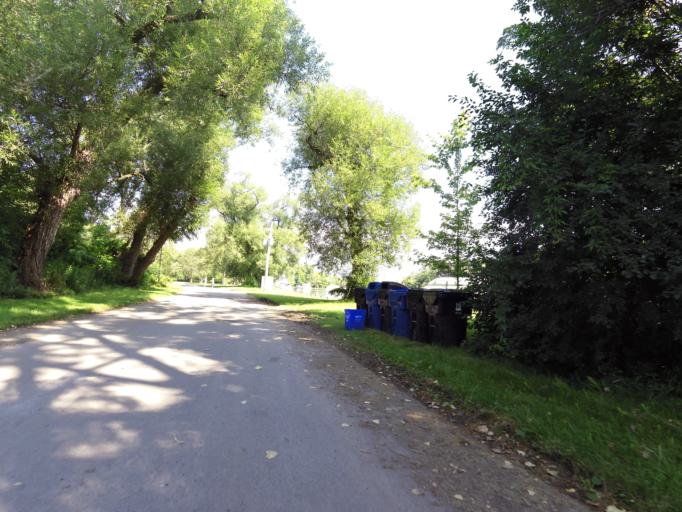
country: CA
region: Ontario
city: Toronto
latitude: 43.6163
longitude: -79.3894
